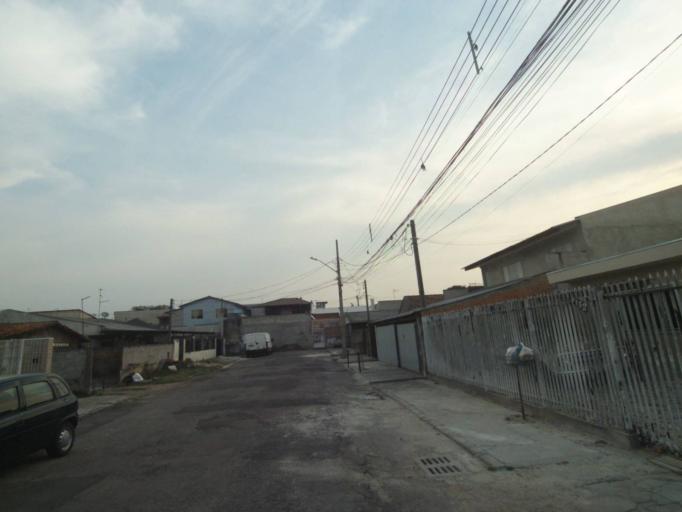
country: BR
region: Parana
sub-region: Sao Jose Dos Pinhais
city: Sao Jose dos Pinhais
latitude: -25.5244
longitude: -49.2707
